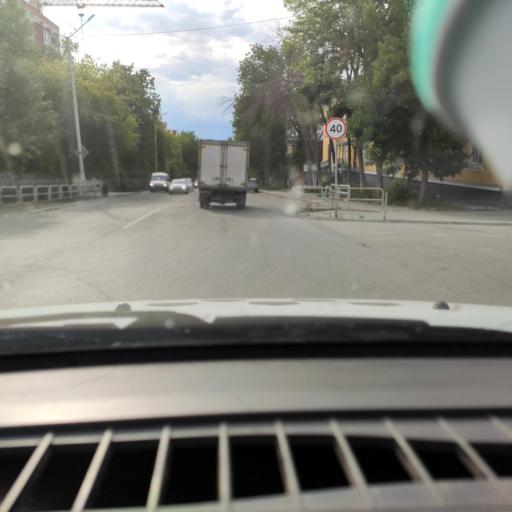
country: RU
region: Chelyabinsk
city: Miass
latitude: 55.0634
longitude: 60.1137
